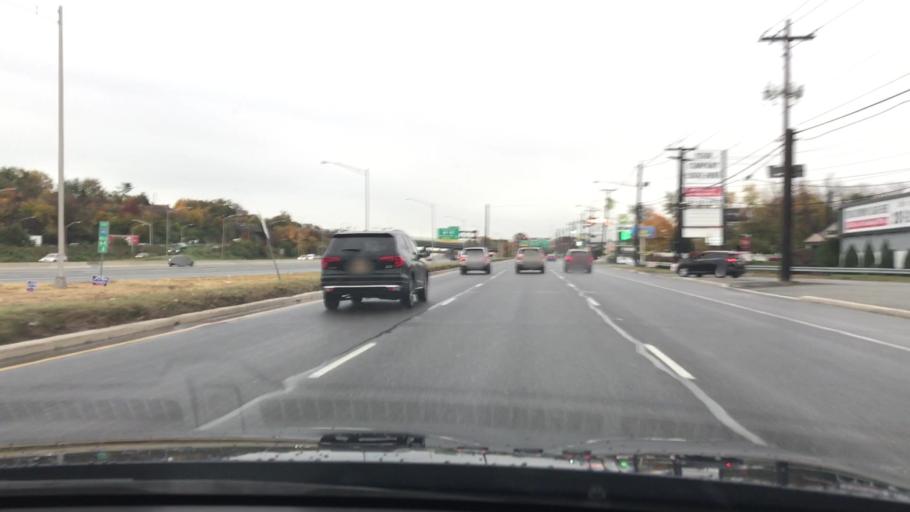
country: US
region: New Jersey
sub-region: Bergen County
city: Lodi
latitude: 40.8821
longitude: -74.0665
